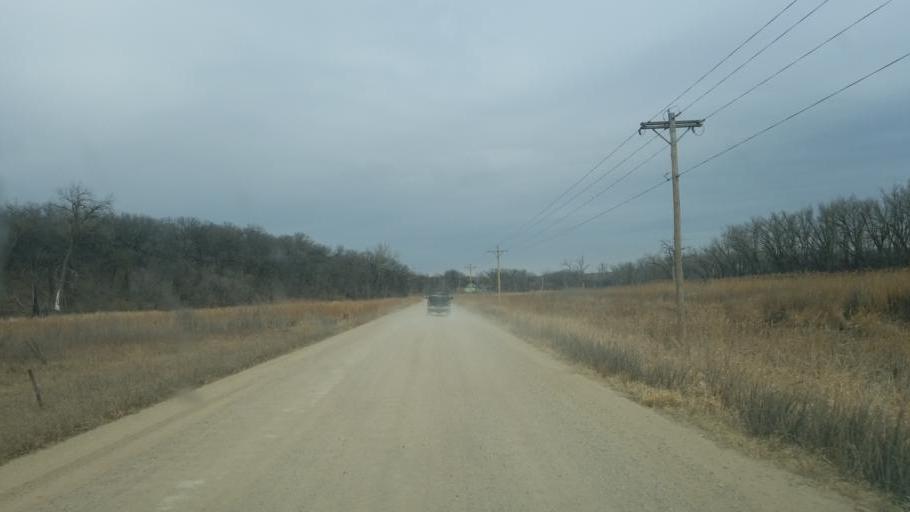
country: US
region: Nebraska
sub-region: Knox County
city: Center
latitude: 42.7198
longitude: -97.9175
